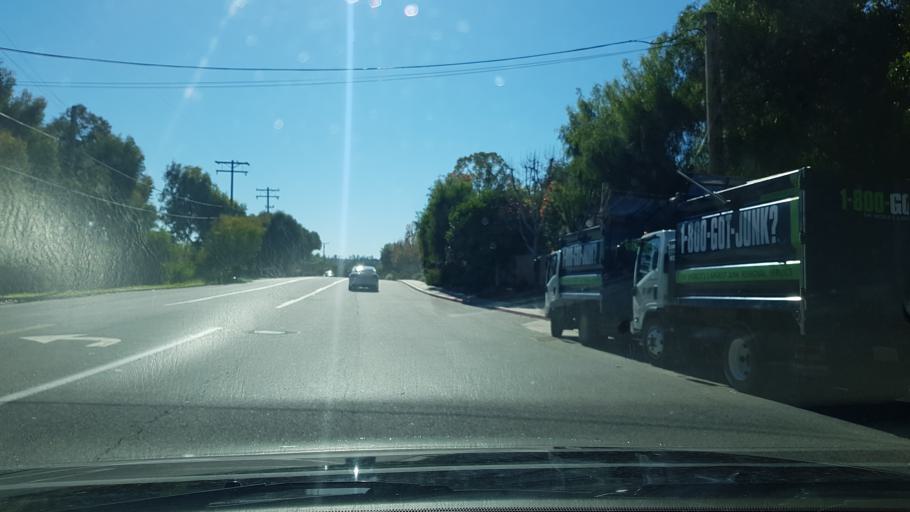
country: US
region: California
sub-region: San Diego County
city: Rancho Santa Fe
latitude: 33.0357
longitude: -117.2393
